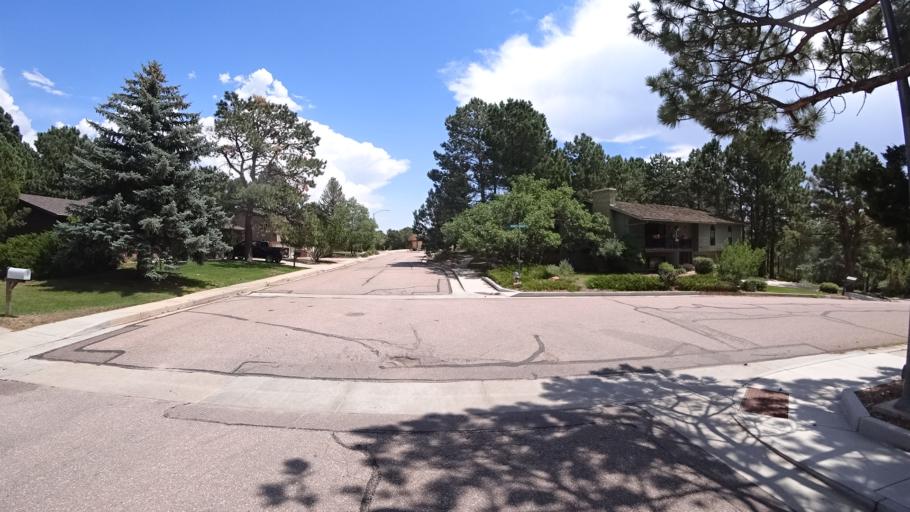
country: US
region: Colorado
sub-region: El Paso County
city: Air Force Academy
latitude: 38.9341
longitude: -104.8255
